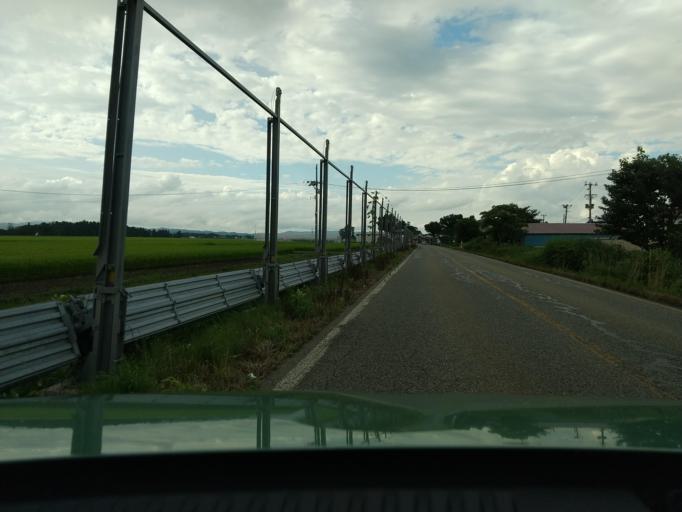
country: JP
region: Akita
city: Yokotemachi
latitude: 39.3098
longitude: 140.4899
